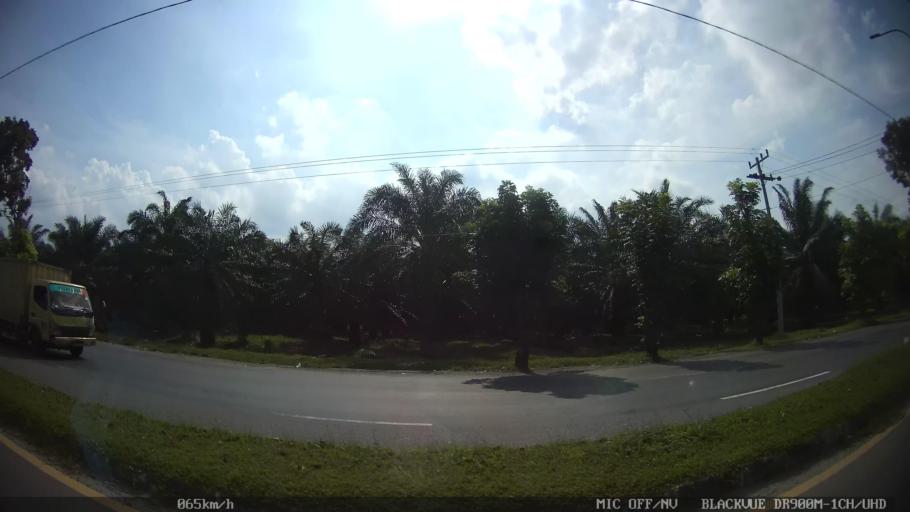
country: ID
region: North Sumatra
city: Binjai
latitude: 3.6486
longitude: 98.5356
